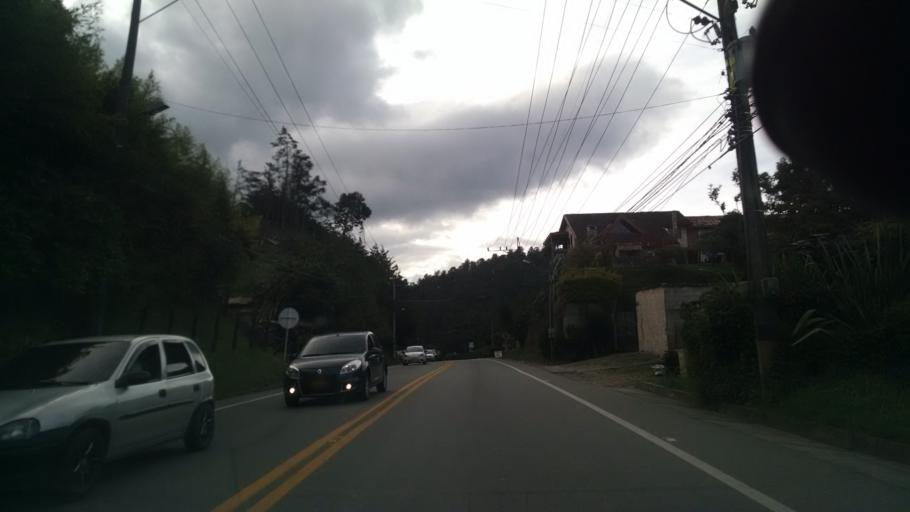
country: CO
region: Antioquia
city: El Retiro
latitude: 6.0927
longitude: -75.4839
